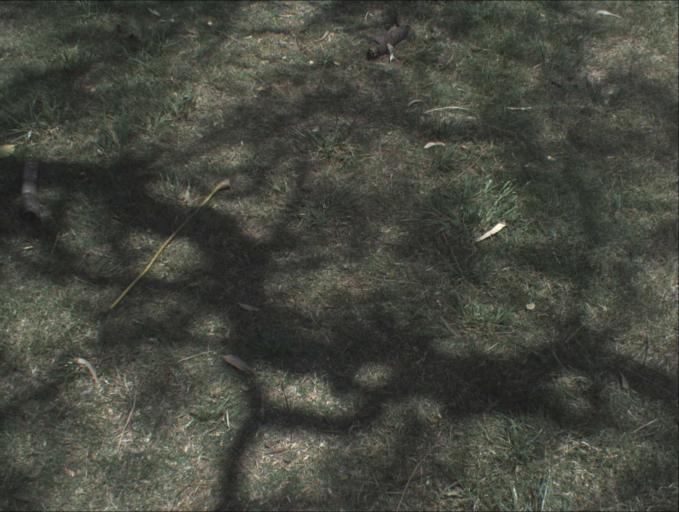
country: AU
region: Queensland
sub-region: Logan
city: Rochedale South
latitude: -27.6008
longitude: 153.1046
